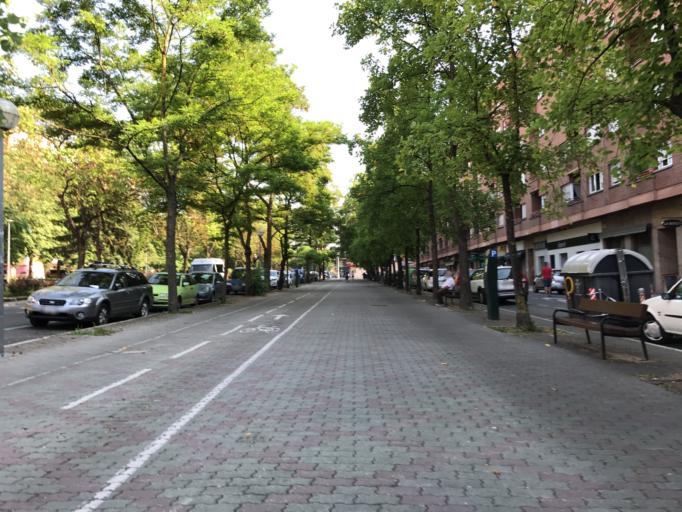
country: ES
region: Basque Country
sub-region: Provincia de Alava
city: Gasteiz / Vitoria
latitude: 42.8517
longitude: -2.6669
